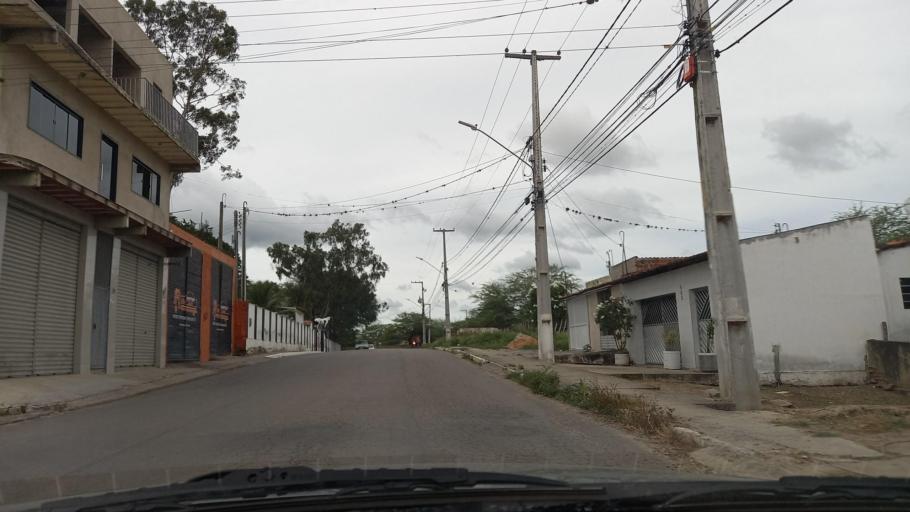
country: BR
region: Pernambuco
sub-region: Gravata
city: Gravata
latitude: -8.2066
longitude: -35.5853
